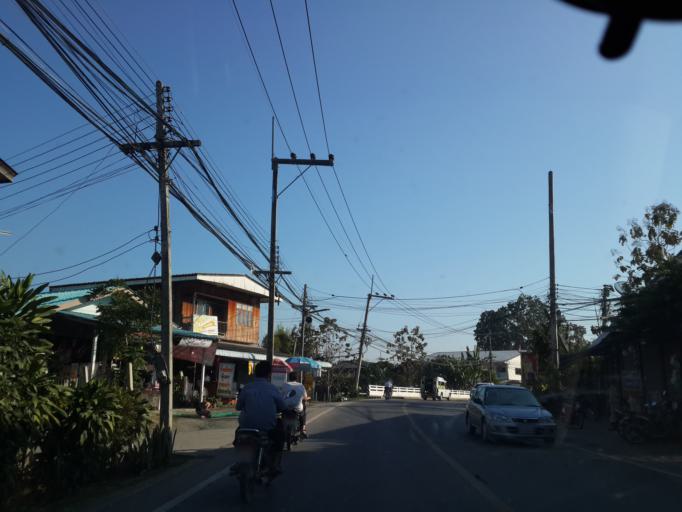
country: TH
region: Chiang Mai
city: San Kamphaeng
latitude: 18.7327
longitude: 99.1279
